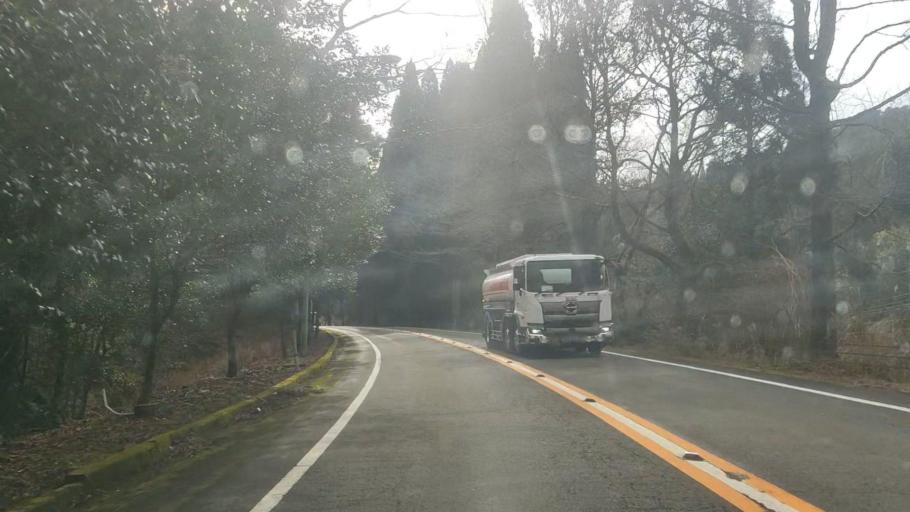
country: JP
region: Kumamoto
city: Hitoyoshi
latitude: 32.1072
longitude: 130.8049
